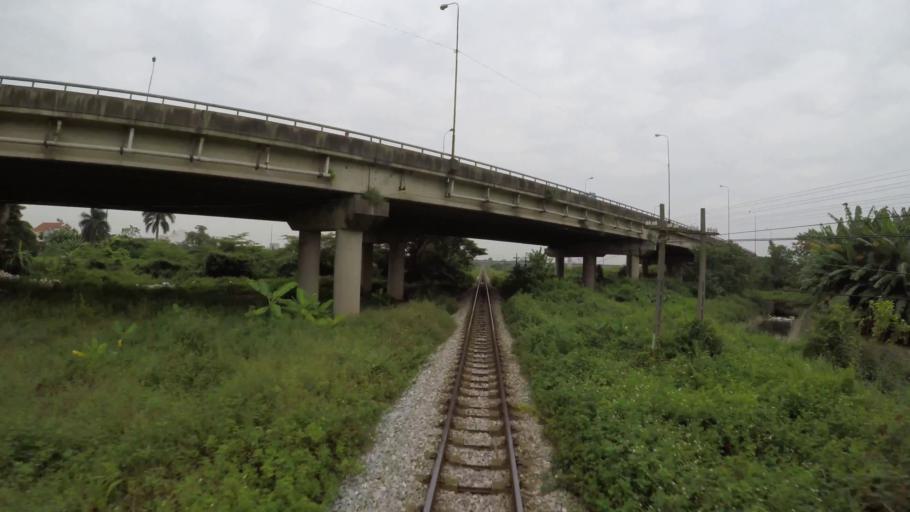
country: VN
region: Hai Phong
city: An Duong
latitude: 20.9115
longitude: 106.5691
